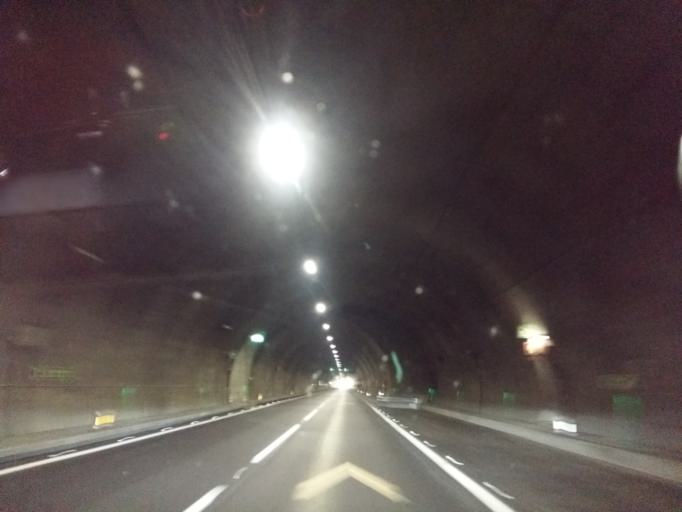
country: PT
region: Castelo Branco
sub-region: Concelho do Fundao
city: Fundao
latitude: 40.1101
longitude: -7.4720
